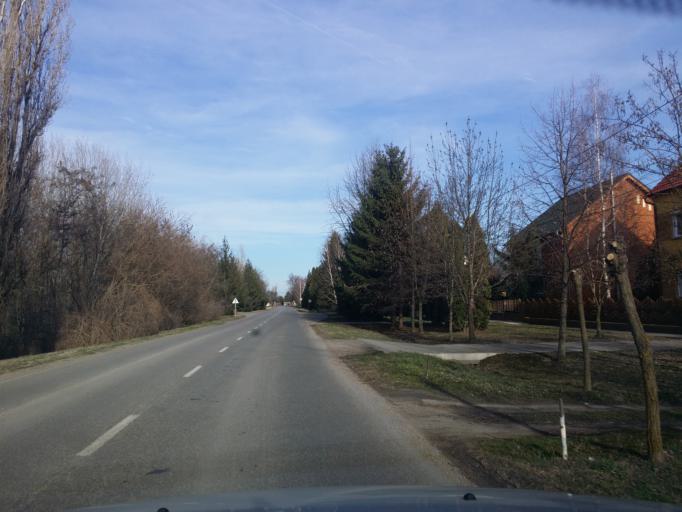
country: HU
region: Tolna
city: Madocsa
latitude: 46.6856
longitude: 18.9446
